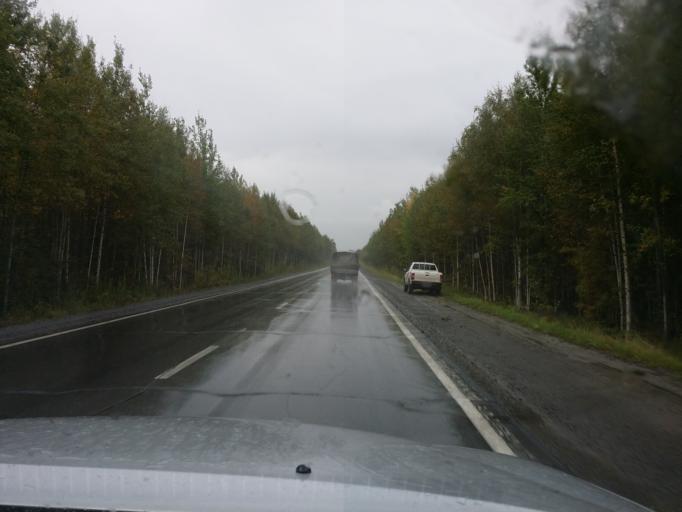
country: RU
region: Khanty-Mansiyskiy Avtonomnyy Okrug
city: Langepas
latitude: 61.1594
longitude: 75.6420
